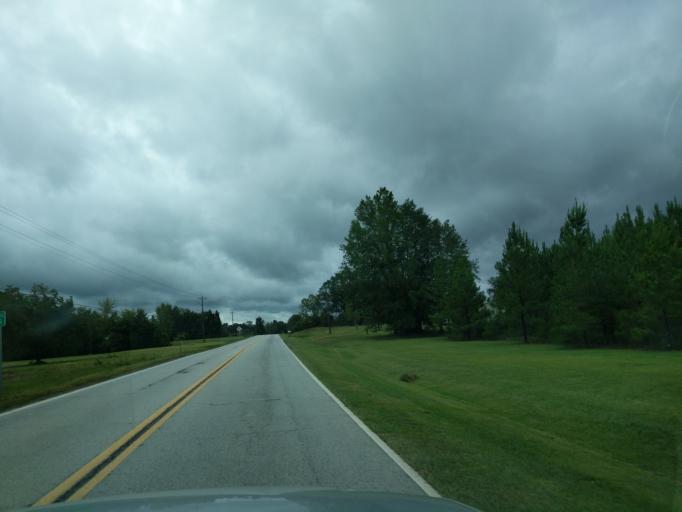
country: US
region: Georgia
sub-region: Elbert County
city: Elberton
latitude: 34.0391
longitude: -82.7978
